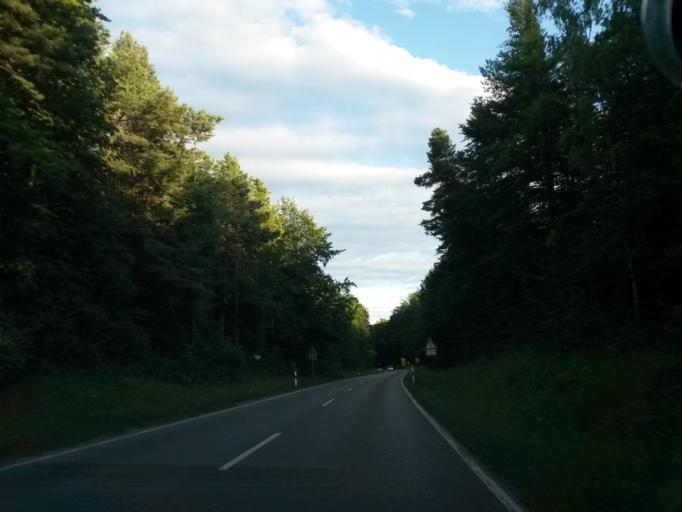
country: DE
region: Baden-Wuerttemberg
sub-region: Karlsruhe Region
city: Birkenfeld
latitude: 48.9000
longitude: 8.6308
